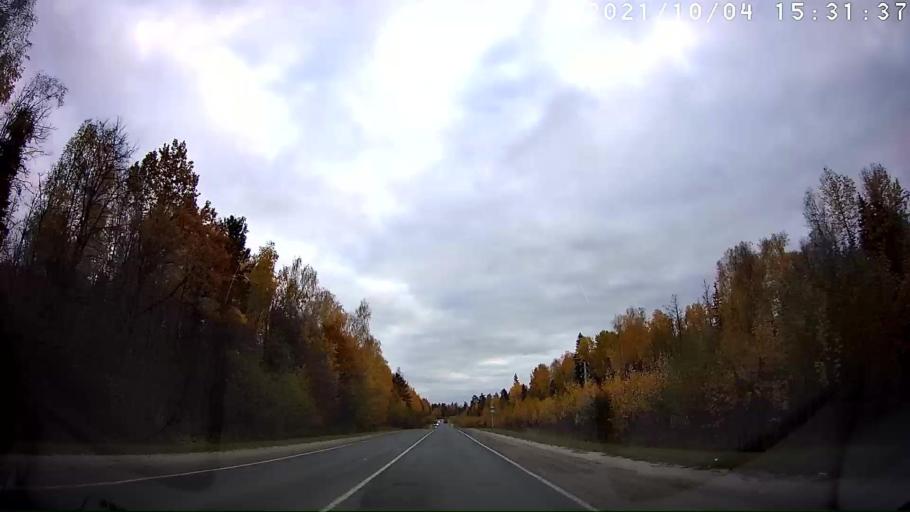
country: RU
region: Mariy-El
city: Yoshkar-Ola
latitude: 56.5775
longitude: 47.9717
